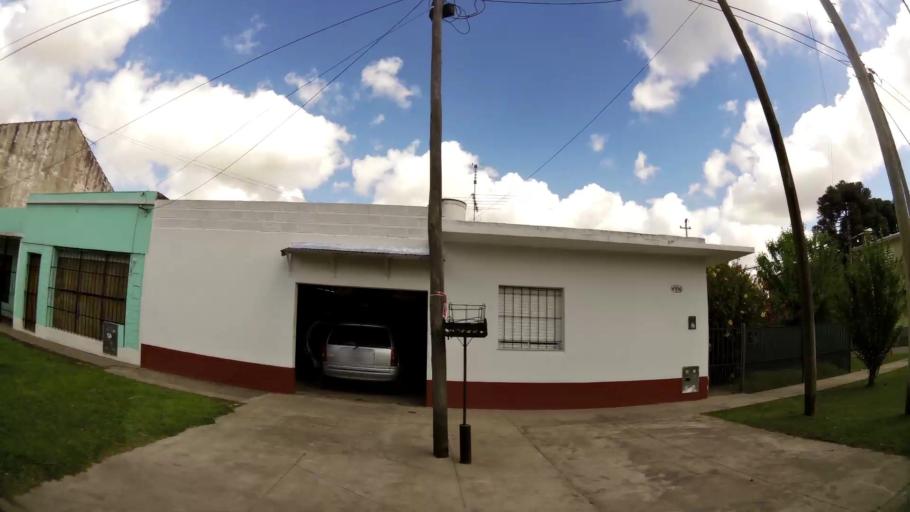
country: AR
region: Buenos Aires
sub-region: Partido de Quilmes
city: Quilmes
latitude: -34.8285
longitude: -58.1872
